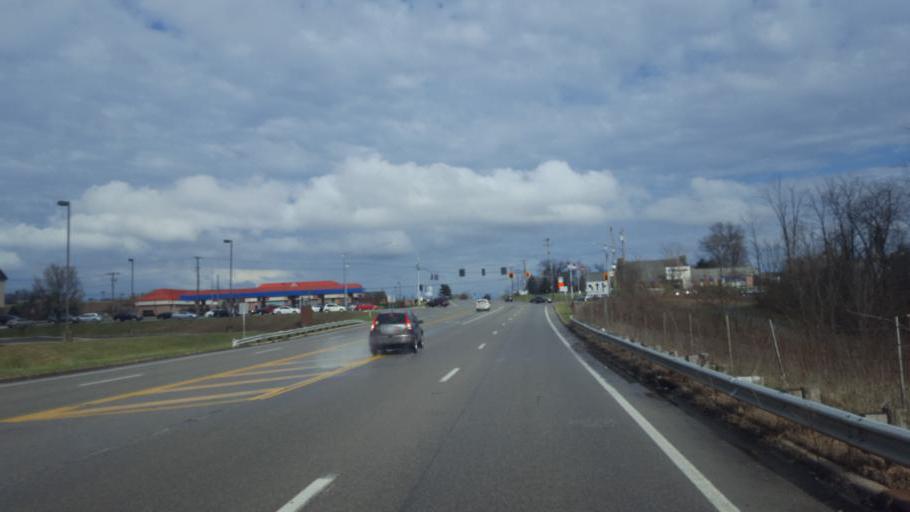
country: US
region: Ohio
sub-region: Delaware County
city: Lewis Center
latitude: 40.1569
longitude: -83.0202
